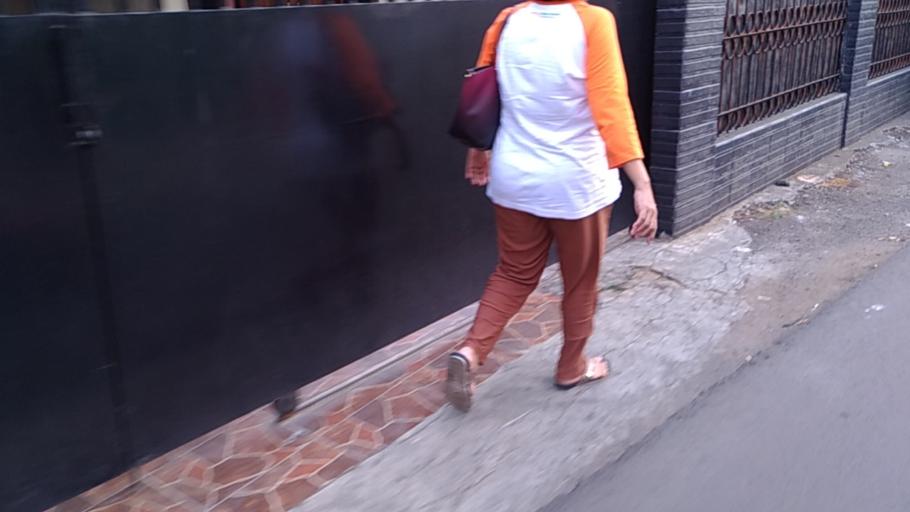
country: ID
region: West Java
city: Depok
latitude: -6.3493
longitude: 106.8758
